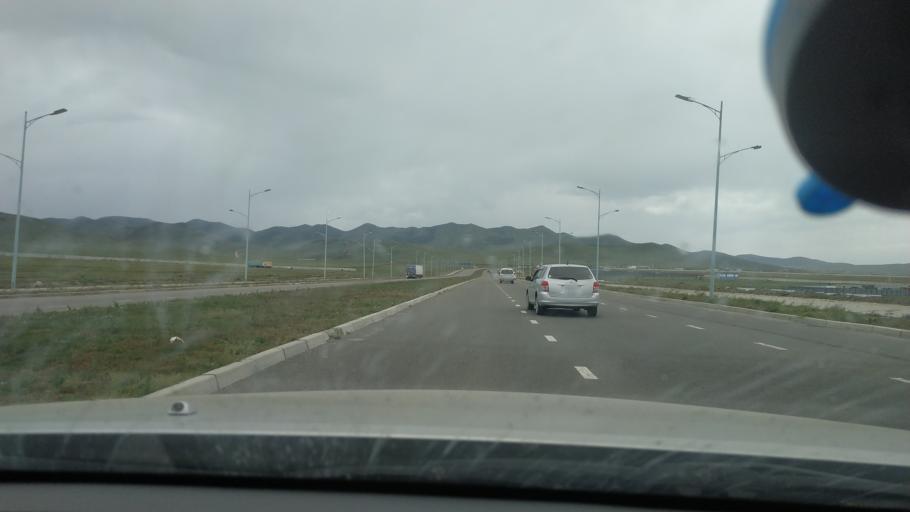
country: MN
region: Ulaanbaatar
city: Ulaanbaatar
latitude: 47.8363
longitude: 106.7886
